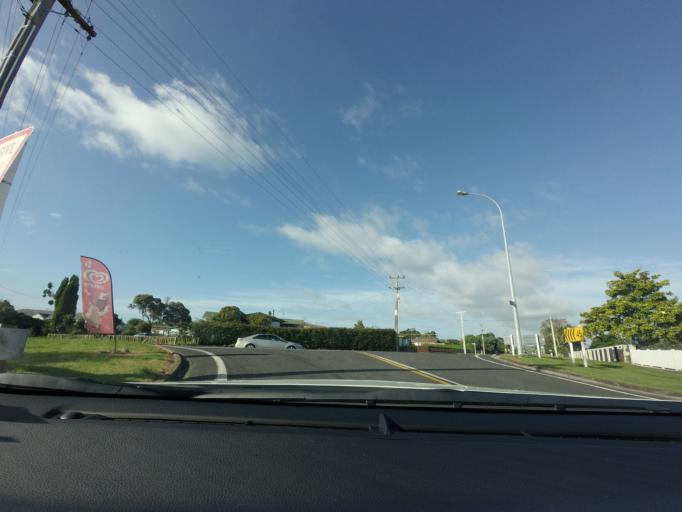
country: NZ
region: Waikato
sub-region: Hauraki District
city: Ngatea
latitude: -37.5000
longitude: 175.4925
